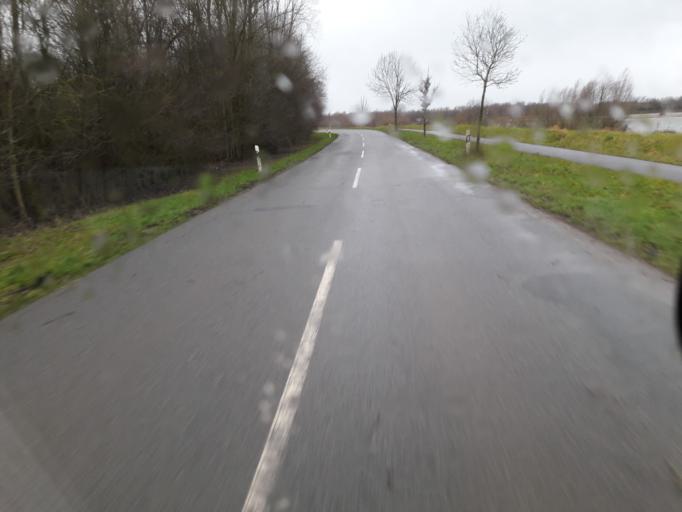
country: DE
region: Lower Saxony
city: Raddestorf
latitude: 52.4280
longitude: 8.9927
